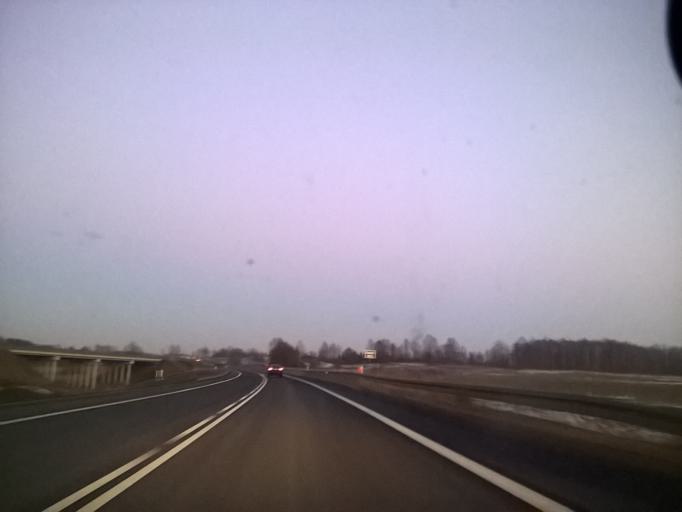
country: PL
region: Warmian-Masurian Voivodeship
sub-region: Powiat olsztynski
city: Biskupiec
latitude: 53.8330
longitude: 20.9140
